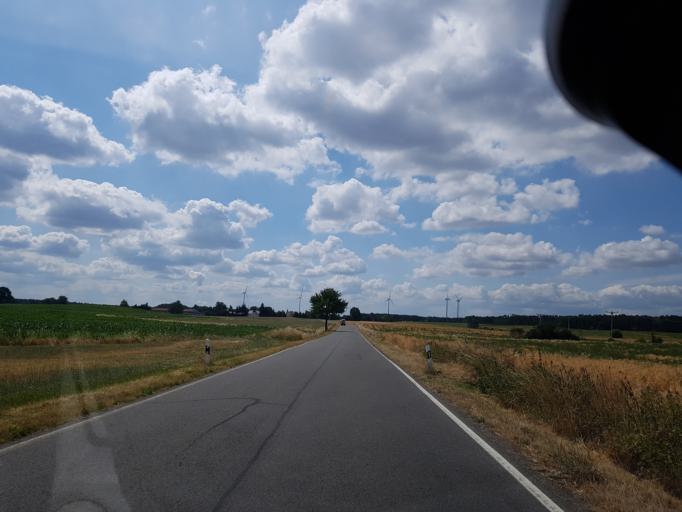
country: DE
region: Brandenburg
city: Drebkau
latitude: 51.6763
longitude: 14.2802
